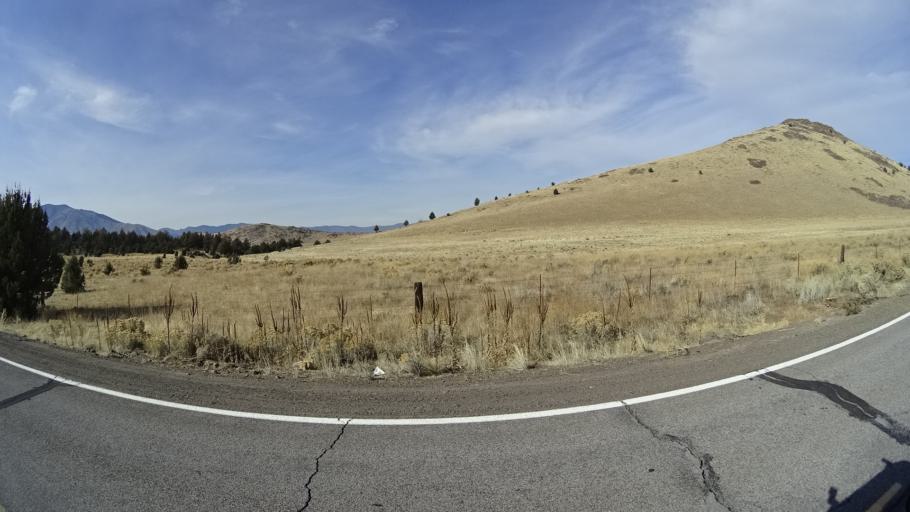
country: US
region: California
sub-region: Siskiyou County
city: Weed
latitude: 41.4900
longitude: -122.4056
